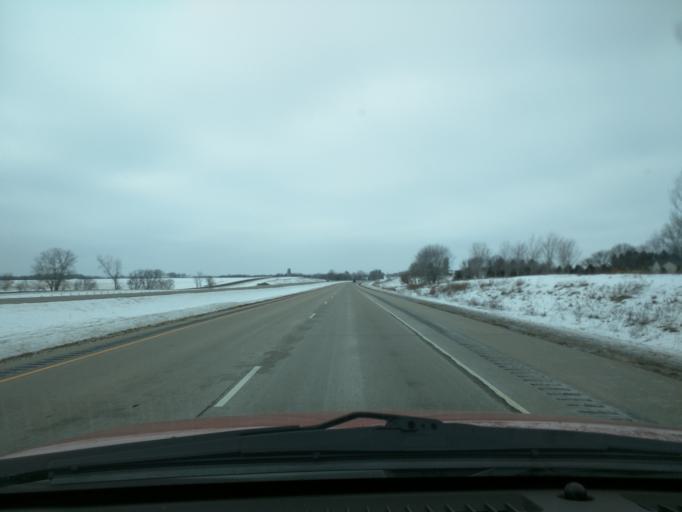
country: US
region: Wisconsin
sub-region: Trempealeau County
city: Trempealeau
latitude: 43.9233
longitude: -91.4905
